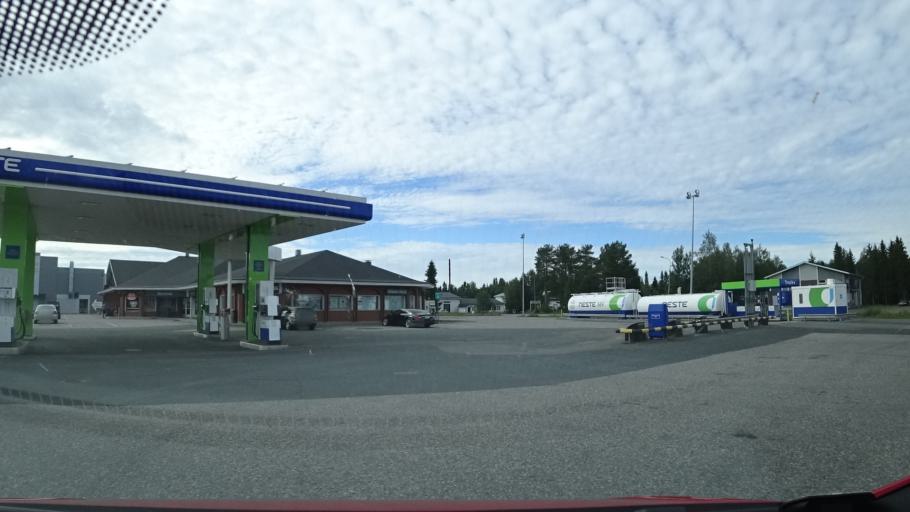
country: FI
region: Lapland
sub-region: Kemi-Tornio
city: Keminmaa
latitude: 65.7999
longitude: 24.5058
